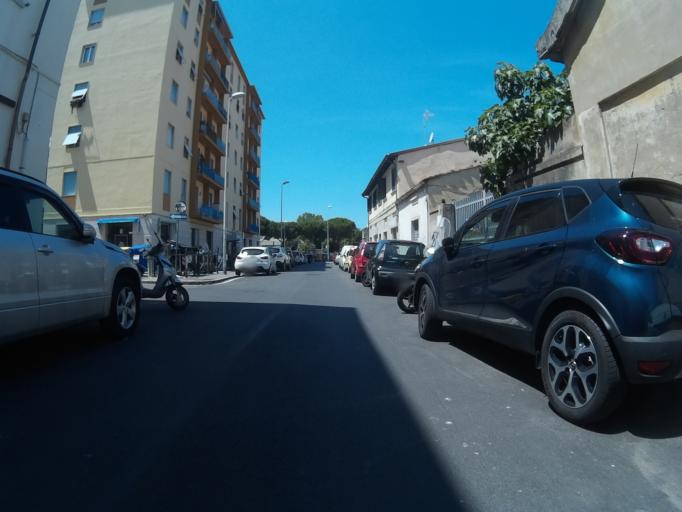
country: IT
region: Tuscany
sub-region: Provincia di Livorno
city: Livorno
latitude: 43.5557
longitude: 10.3223
